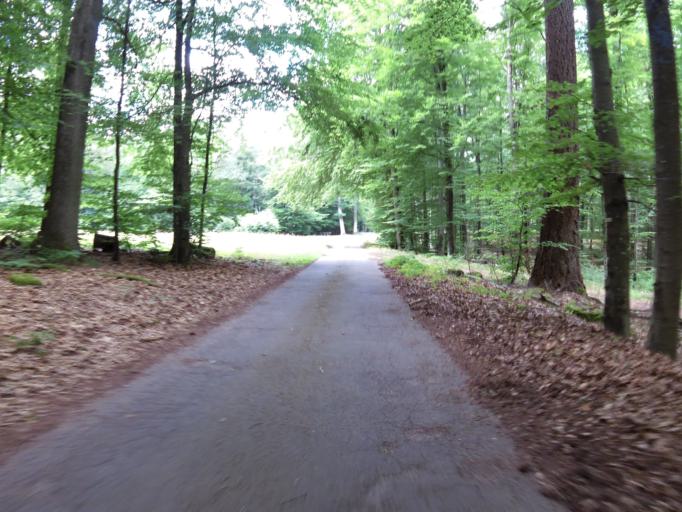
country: DE
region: Rheinland-Pfalz
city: Waldleiningen
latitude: 49.3938
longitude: 7.9115
